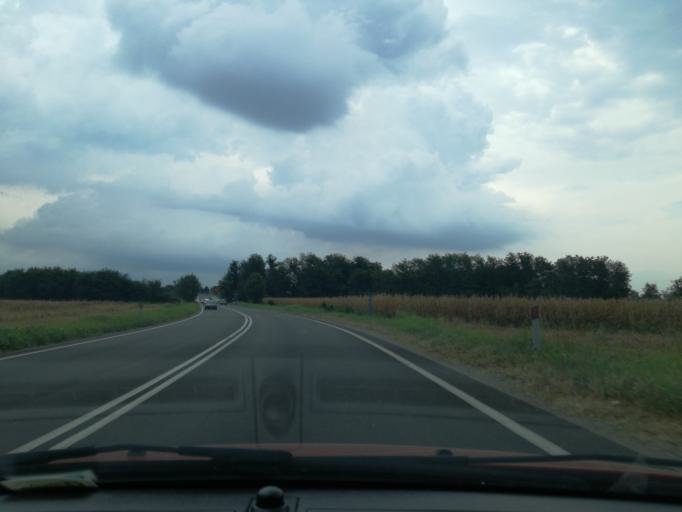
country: IT
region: Lombardy
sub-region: Provincia di Monza e Brianza
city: Velasca
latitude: 45.6391
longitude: 9.3565
